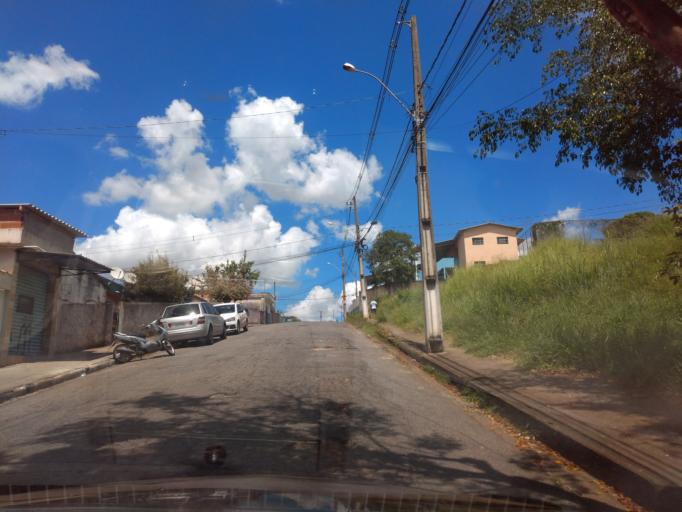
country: BR
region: Minas Gerais
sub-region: Tres Coracoes
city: Tres Coracoes
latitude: -21.6863
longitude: -45.2523
